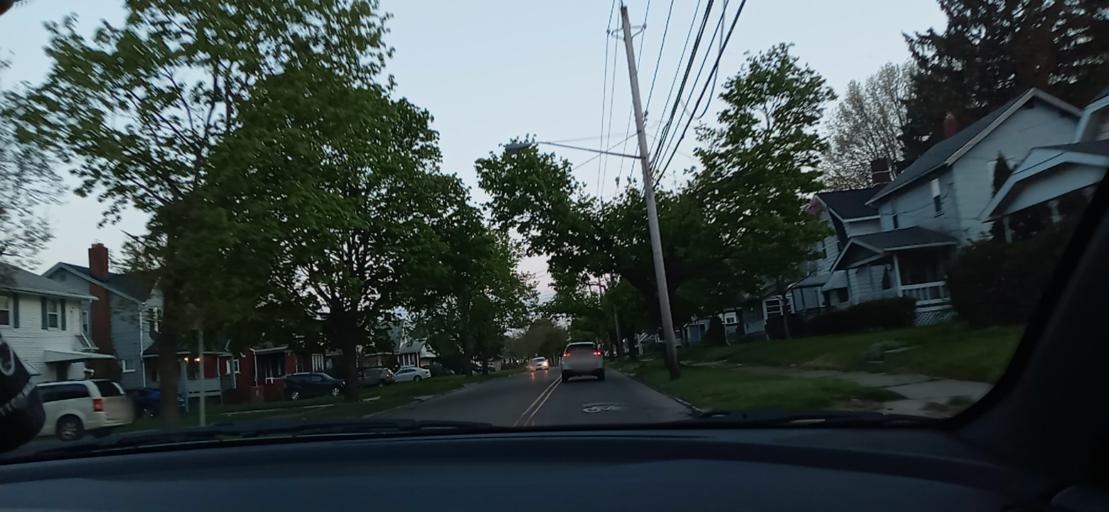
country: US
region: Ohio
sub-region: Summit County
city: Akron
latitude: 41.0494
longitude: -81.5102
